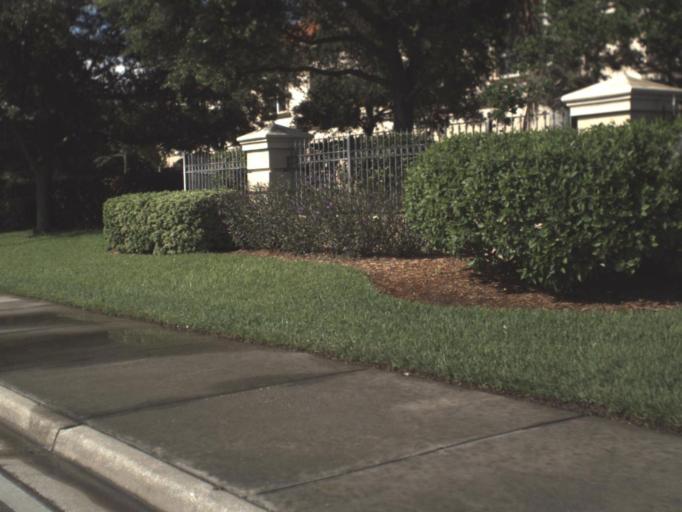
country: US
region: Florida
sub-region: Sarasota County
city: Sarasota
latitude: 27.3501
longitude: -82.5470
